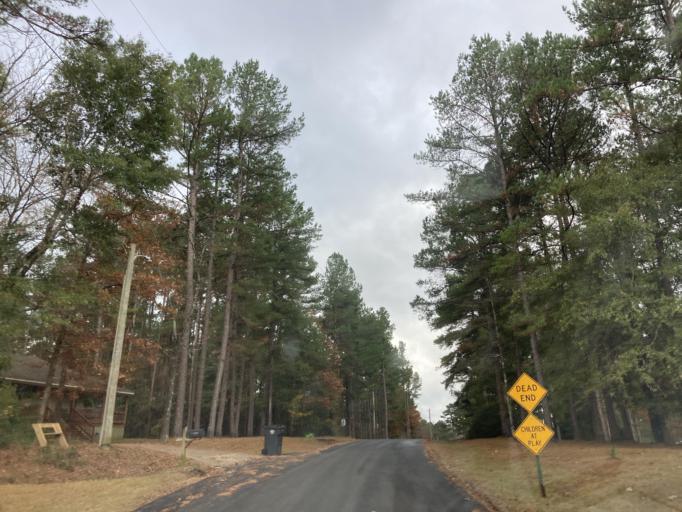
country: US
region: Mississippi
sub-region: Lamar County
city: Purvis
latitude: 31.1389
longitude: -89.5412
